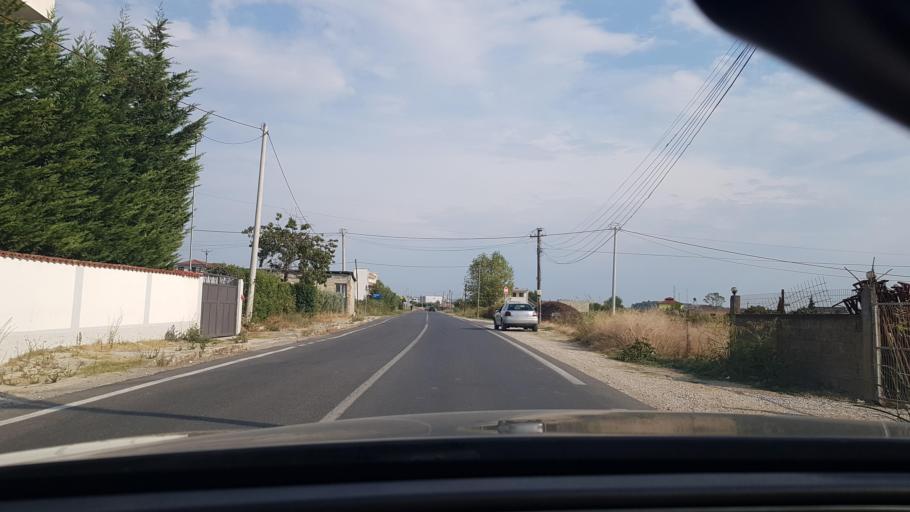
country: AL
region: Durres
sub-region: Rrethi i Durresit
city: Manze
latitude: 41.4507
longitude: 19.5703
